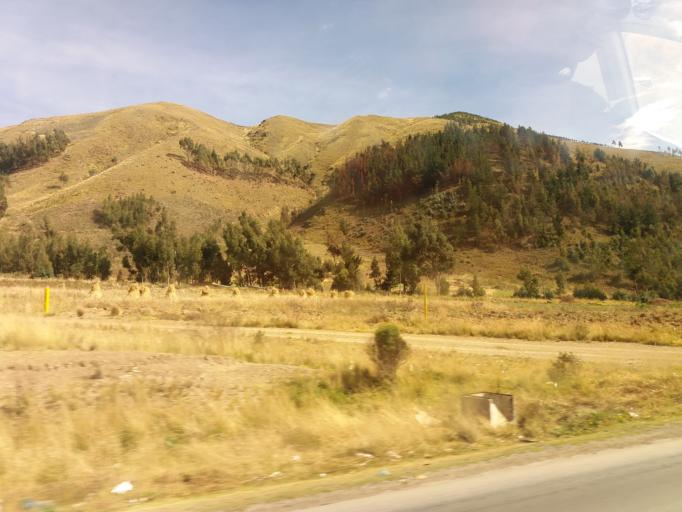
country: BO
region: Cochabamba
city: Colomi
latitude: -17.3820
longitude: -65.8344
